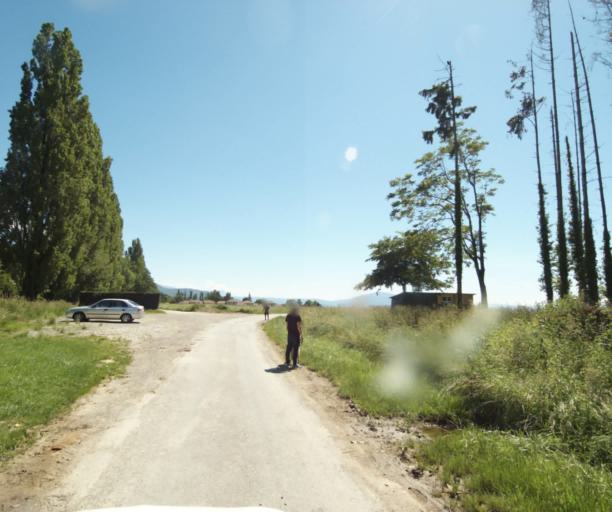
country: FR
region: Rhone-Alpes
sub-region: Departement de la Haute-Savoie
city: Loisin
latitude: 46.2817
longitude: 6.3250
